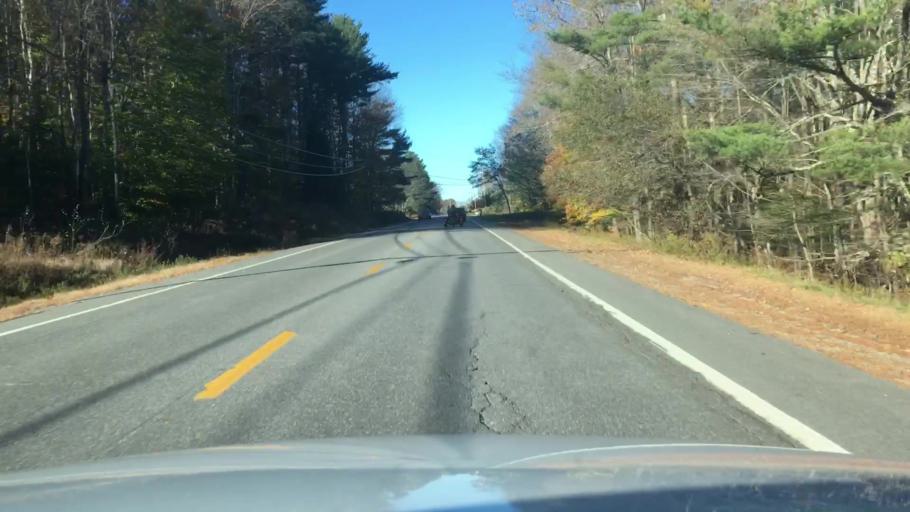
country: US
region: Maine
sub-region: Sagadahoc County
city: Topsham
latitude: 44.0389
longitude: -69.9426
